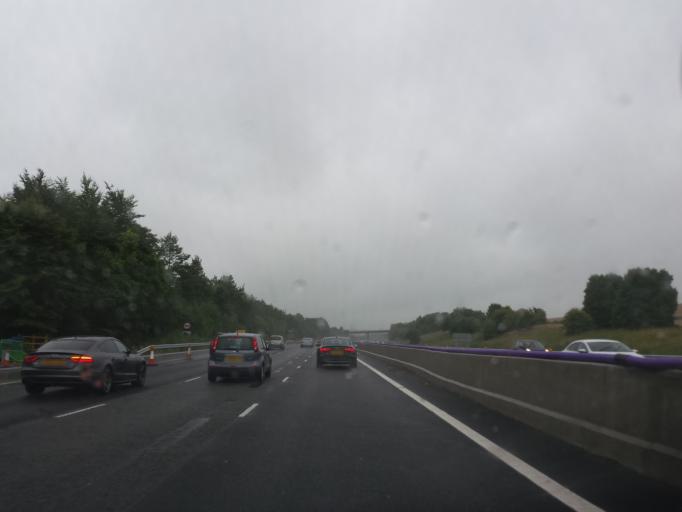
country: GB
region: England
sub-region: Derbyshire
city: Tibshelf
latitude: 53.1696
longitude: -1.3245
